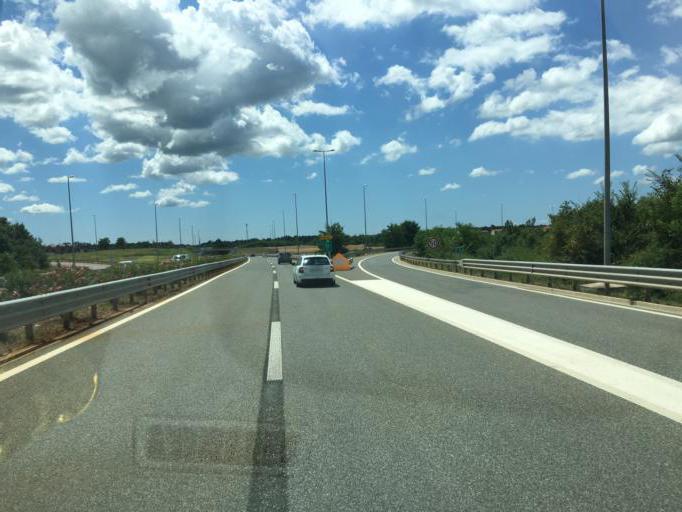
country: HR
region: Istarska
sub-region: Grad Porec
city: Porec
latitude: 45.2189
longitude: 13.7226
